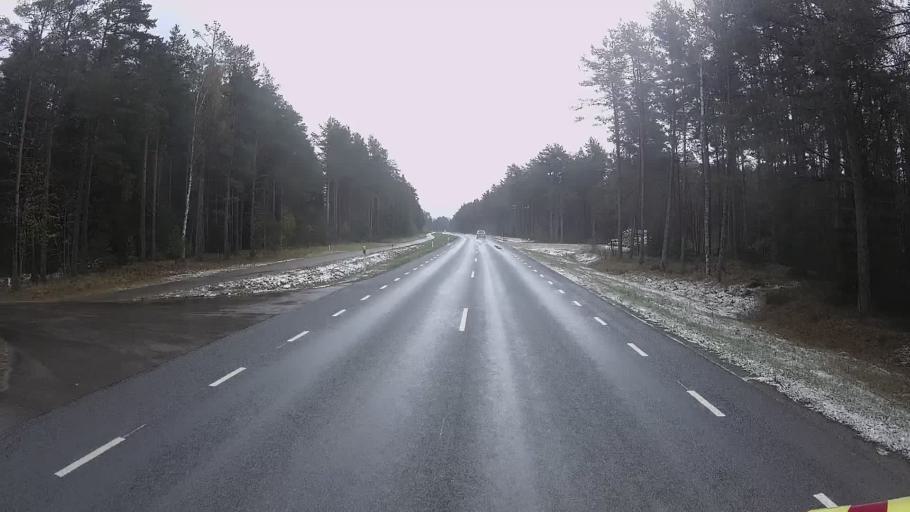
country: EE
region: Hiiumaa
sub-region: Kaerdla linn
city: Kardla
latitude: 58.9976
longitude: 22.7086
